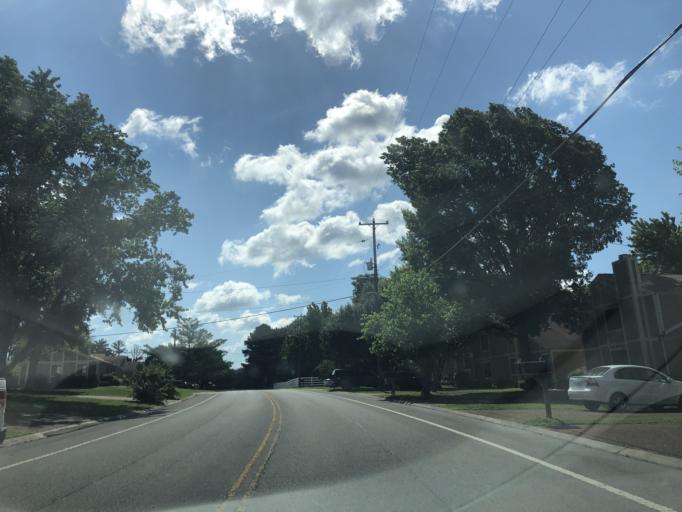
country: US
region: Tennessee
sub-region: Davidson County
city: Belle Meade
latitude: 36.0691
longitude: -86.9435
